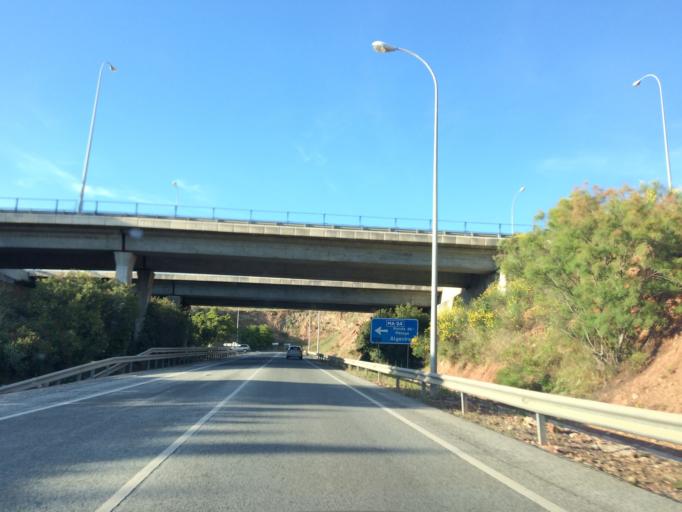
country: ES
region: Andalusia
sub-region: Provincia de Malaga
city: Totalan
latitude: 36.7236
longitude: -4.3433
